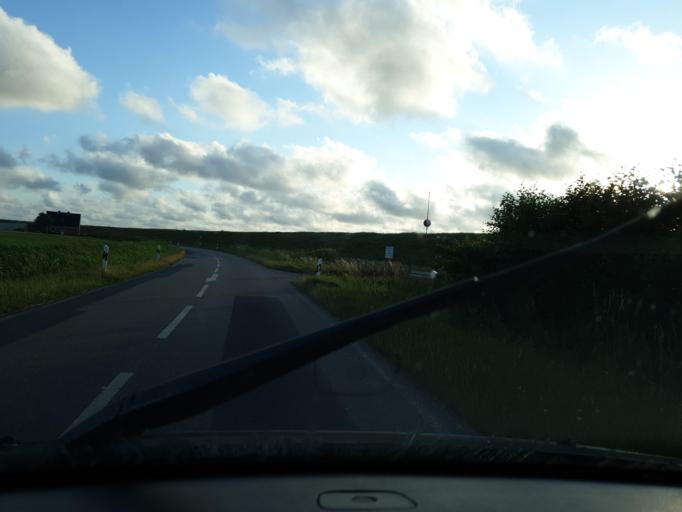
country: DE
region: Schleswig-Holstein
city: Busenwurth
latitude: 54.0585
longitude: 9.0169
